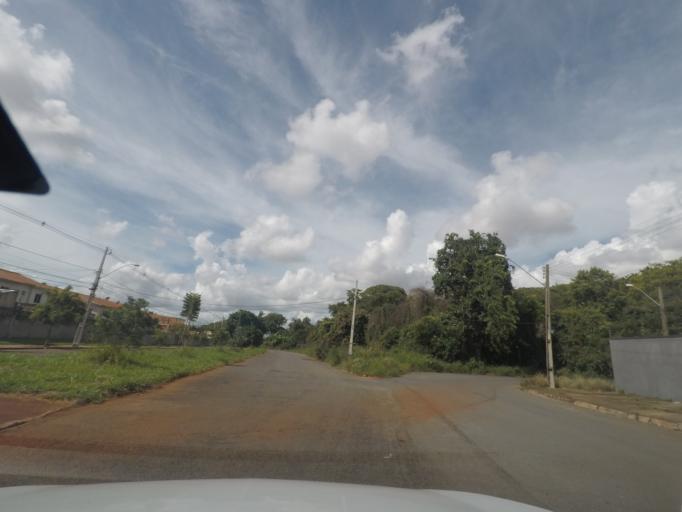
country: BR
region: Goias
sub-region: Goiania
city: Goiania
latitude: -16.7149
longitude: -49.3442
